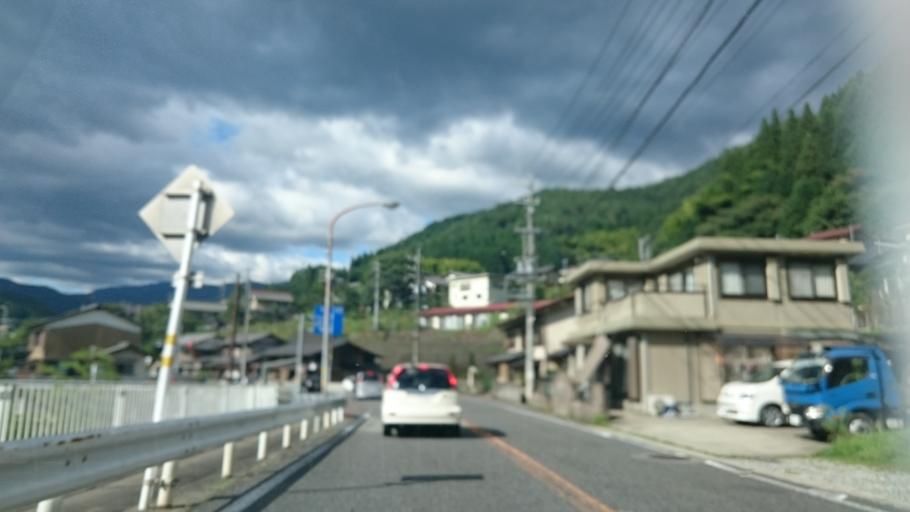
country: JP
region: Gifu
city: Gujo
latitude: 35.7791
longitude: 137.2540
